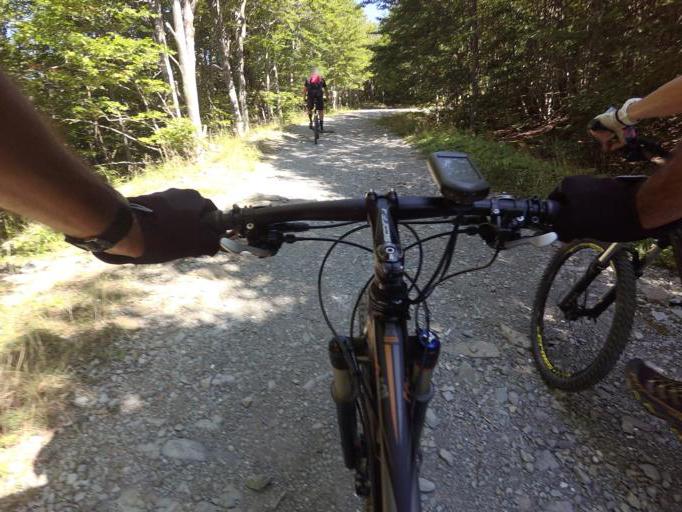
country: IT
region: Emilia-Romagna
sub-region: Provincia di Modena
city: Montecreto
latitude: 44.2303
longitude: 10.7303
